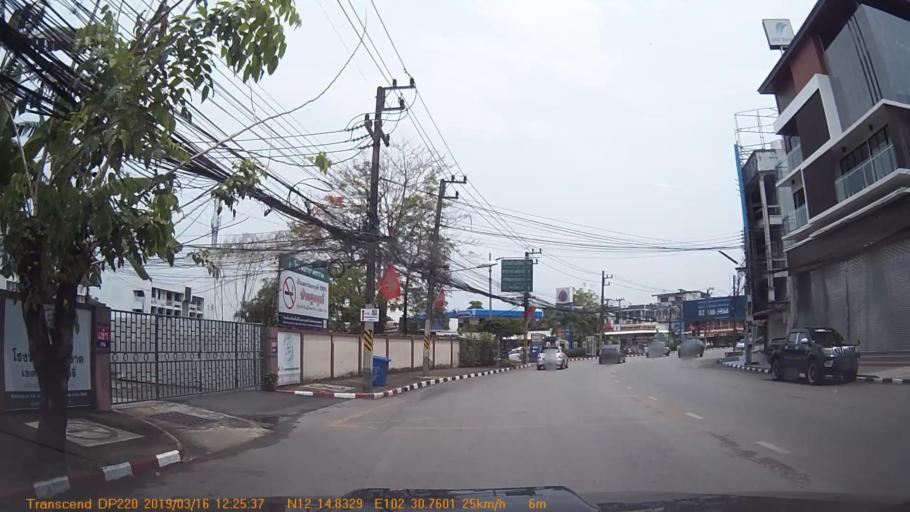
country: TH
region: Trat
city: Trat
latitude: 12.2473
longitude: 102.5128
